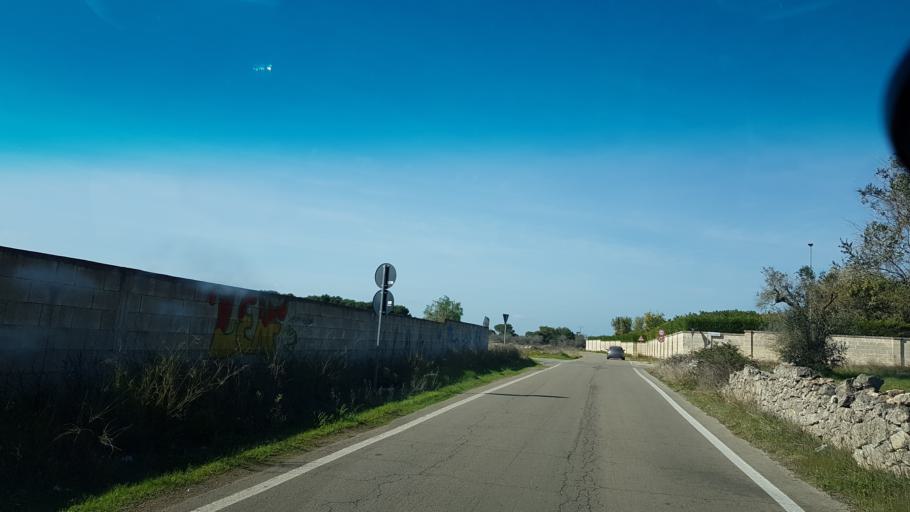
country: IT
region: Apulia
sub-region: Provincia di Lecce
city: Arnesano
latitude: 40.3518
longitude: 18.1044
